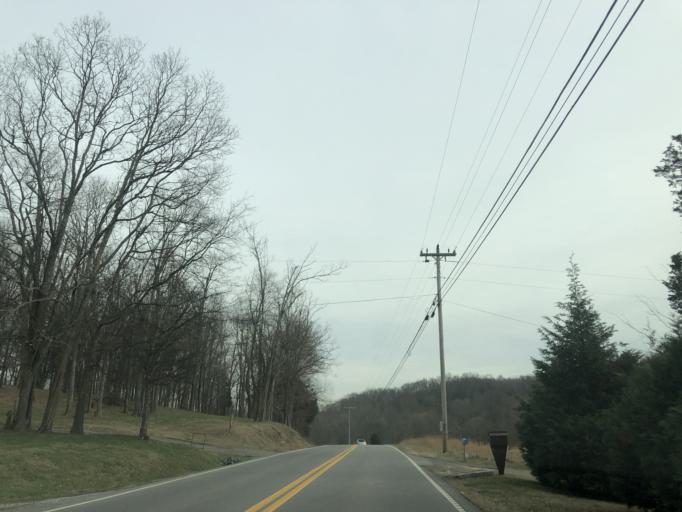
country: US
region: Tennessee
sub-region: Sumner County
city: White House
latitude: 36.4689
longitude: -86.5659
